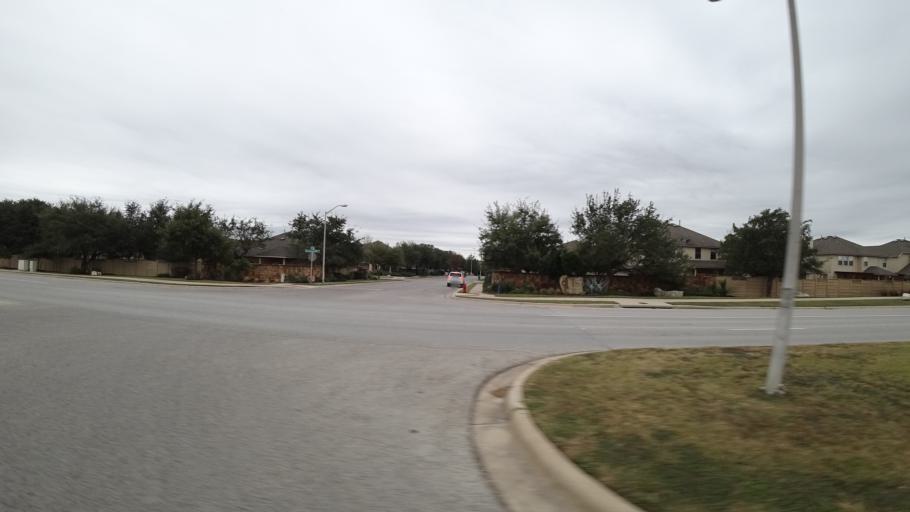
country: US
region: Texas
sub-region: Williamson County
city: Cedar Park
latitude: 30.4883
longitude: -97.8582
